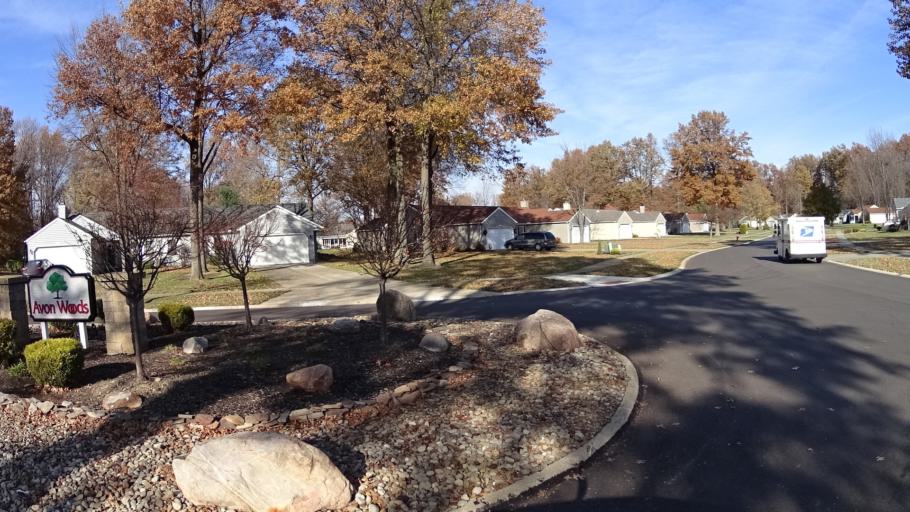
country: US
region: Ohio
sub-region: Lorain County
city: Avon
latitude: 41.4591
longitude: -82.0343
